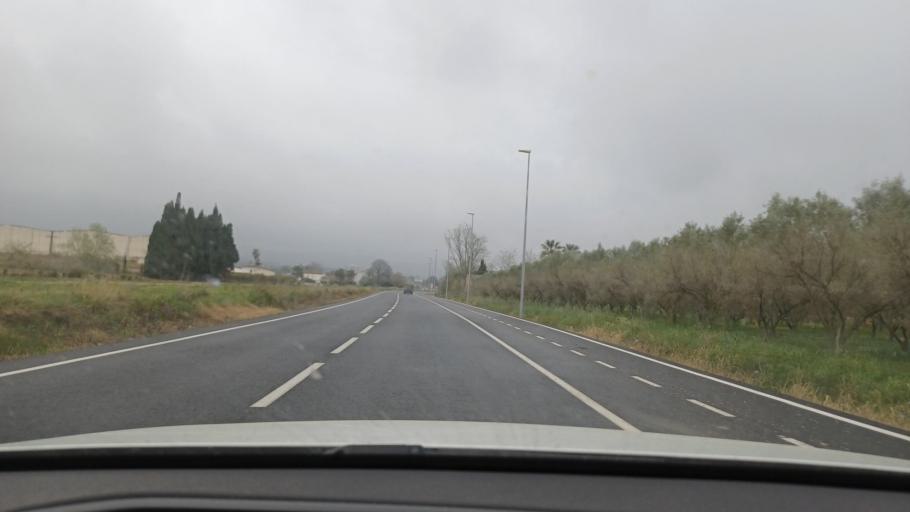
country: ES
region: Catalonia
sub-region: Provincia de Tarragona
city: Tortosa
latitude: 40.8077
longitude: 0.5018
